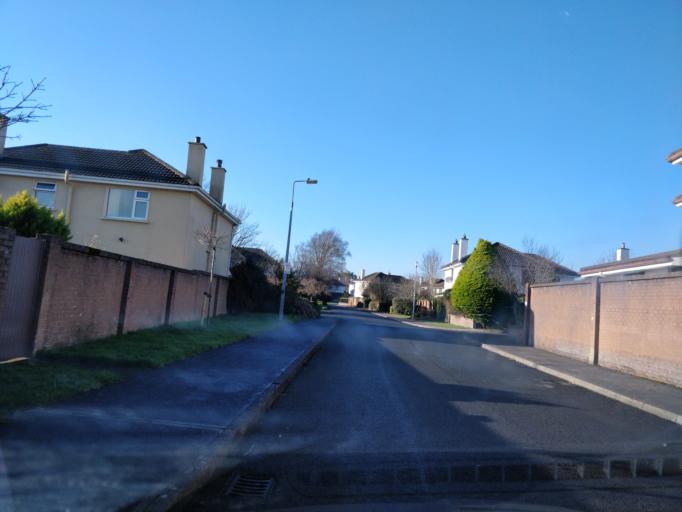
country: IE
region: Connaught
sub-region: County Galway
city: Bearna
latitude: 53.2611
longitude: -9.1181
